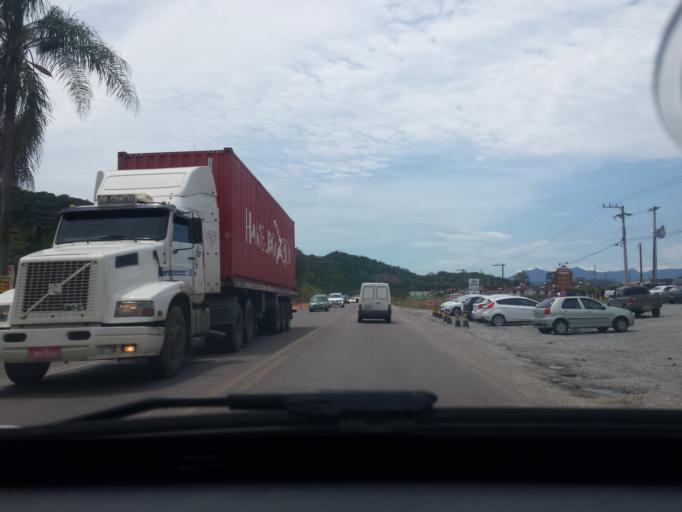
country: BR
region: Santa Catarina
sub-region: Gaspar
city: Gaspar
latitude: -26.8985
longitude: -48.9857
